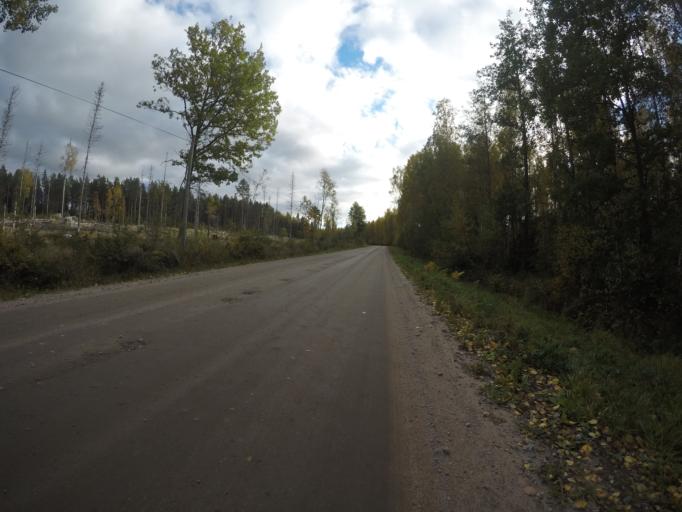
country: SE
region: Vaestmanland
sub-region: Arboga Kommun
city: Tyringe
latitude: 59.3777
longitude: 15.9487
